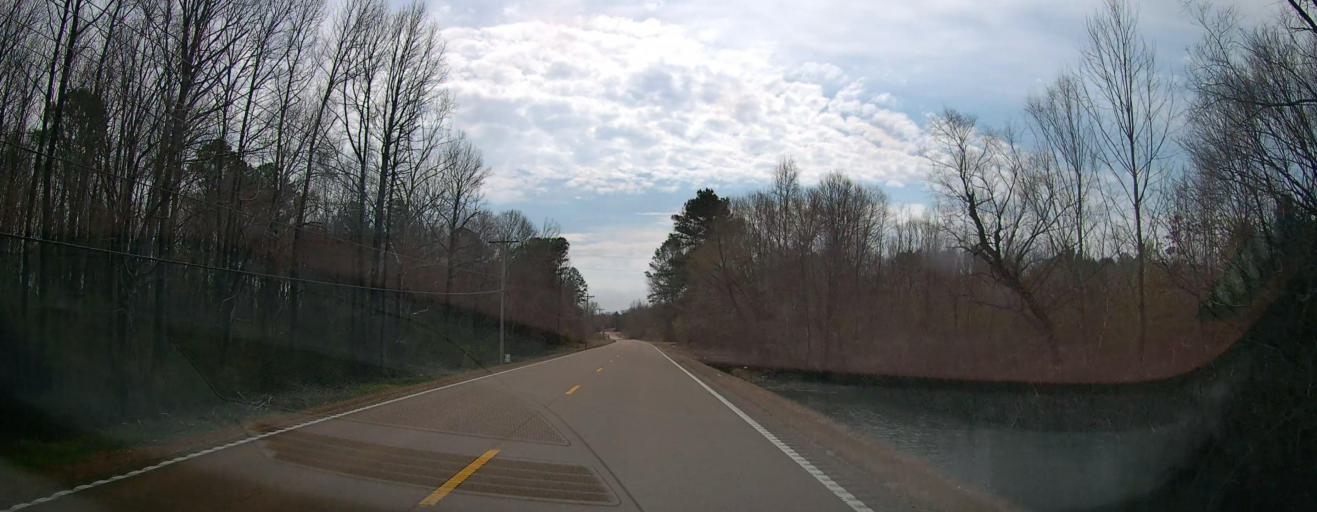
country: US
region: Mississippi
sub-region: Marshall County
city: Holly Springs
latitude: 34.7280
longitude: -89.4184
